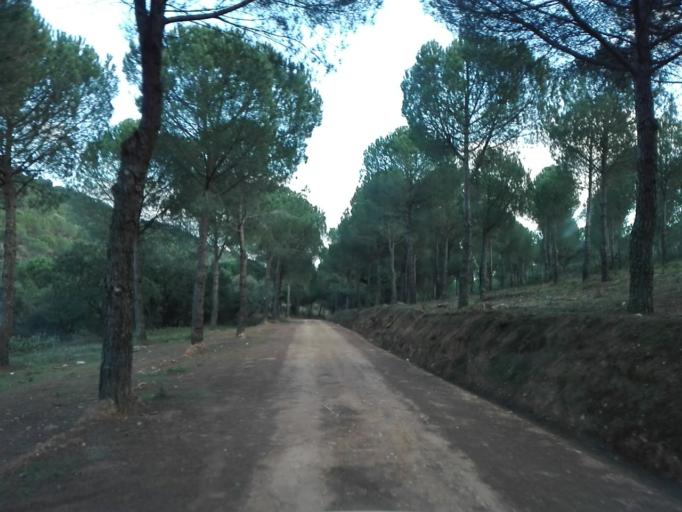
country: ES
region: Extremadura
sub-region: Provincia de Badajoz
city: Trasierra
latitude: 38.1813
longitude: -5.9803
